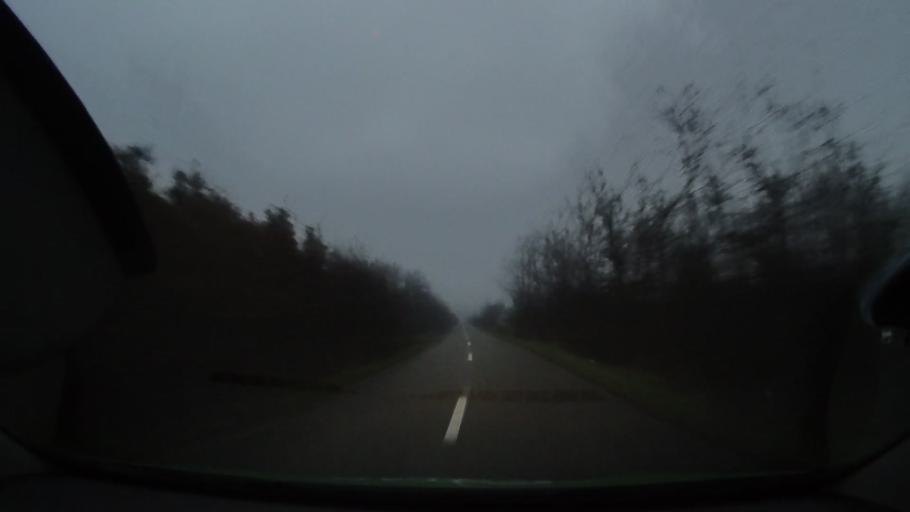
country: RO
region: Arad
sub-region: Comuna Beliu
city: Beliu
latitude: 46.4837
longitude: 22.0135
